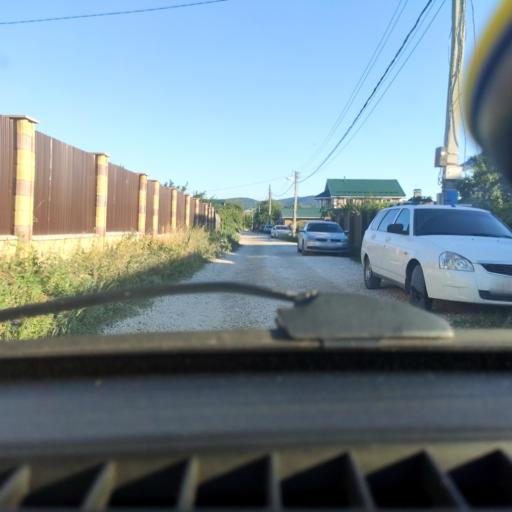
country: RU
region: Samara
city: Zhigulevsk
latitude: 53.4666
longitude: 49.5924
